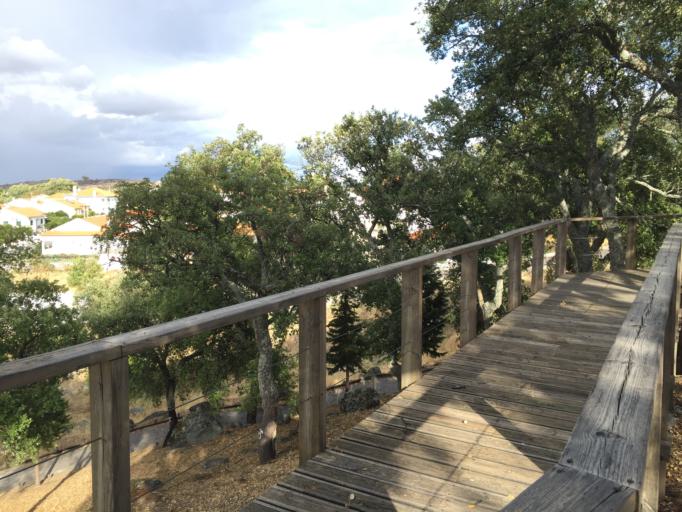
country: PT
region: Portalegre
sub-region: Marvao
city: Marvao
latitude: 39.4122
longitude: -7.3502
